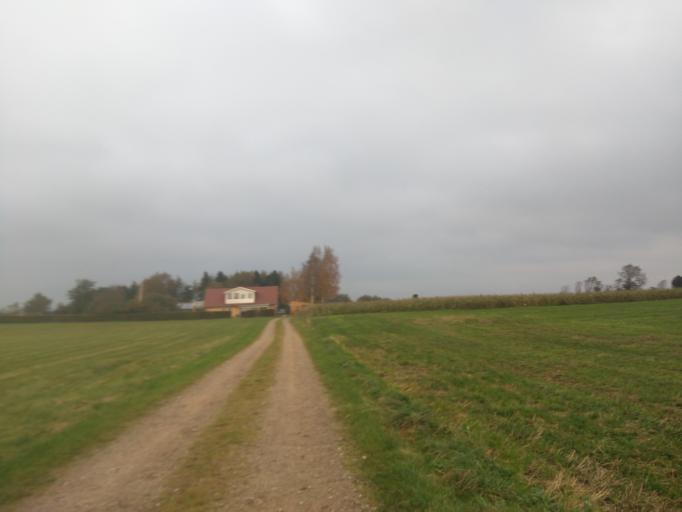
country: DK
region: Central Jutland
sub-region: Silkeborg Kommune
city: Silkeborg
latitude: 56.2484
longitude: 9.5167
